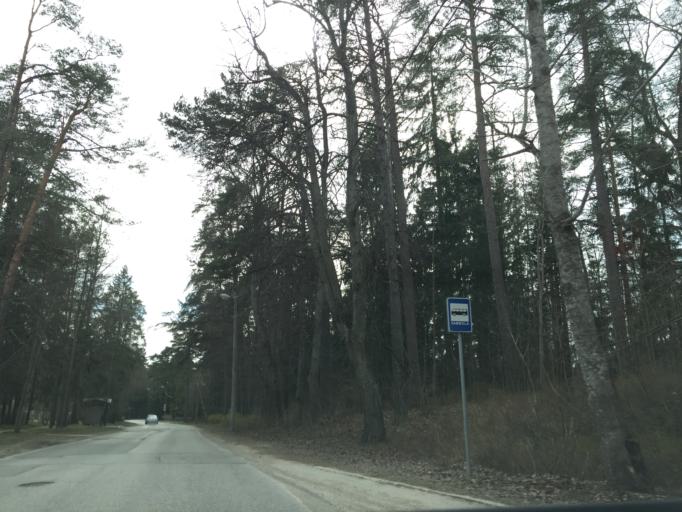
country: EE
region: Ida-Virumaa
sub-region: Narva-Joesuu linn
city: Narva-Joesuu
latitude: 59.4495
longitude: 28.0246
